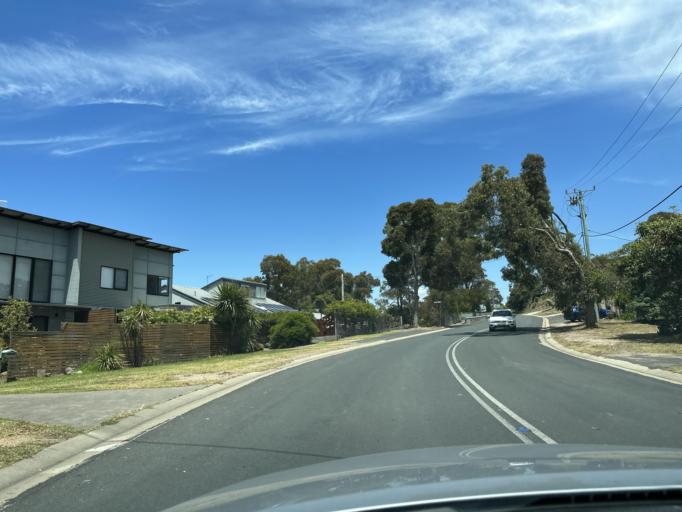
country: AU
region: New South Wales
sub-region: Bega Valley
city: Merimbula
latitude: -36.8913
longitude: 149.9019
